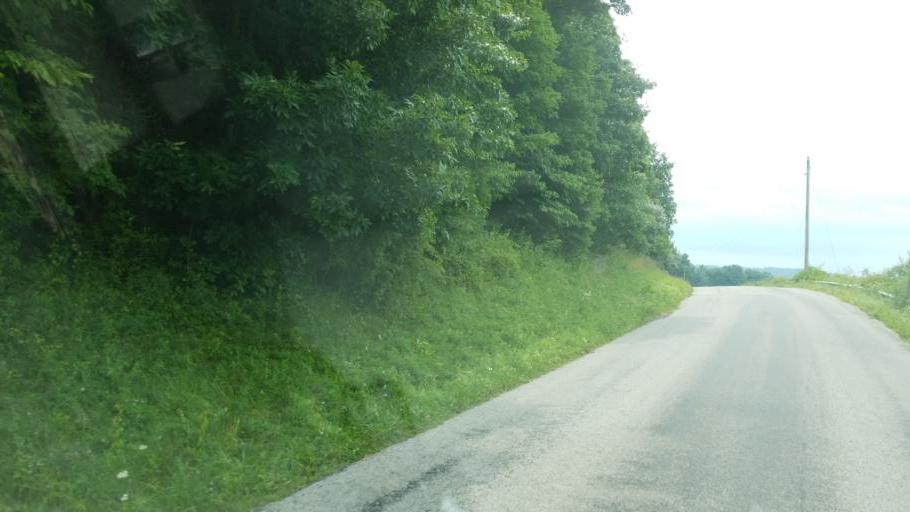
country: US
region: Ohio
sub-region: Licking County
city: Utica
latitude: 40.1678
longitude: -82.4284
